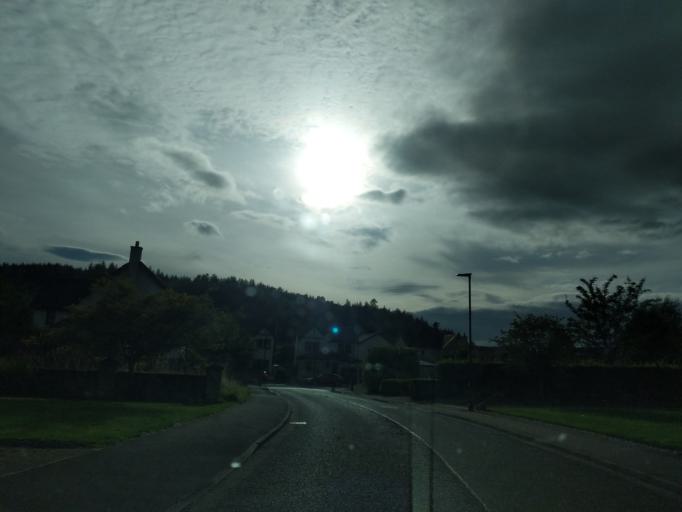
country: GB
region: Scotland
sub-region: The Scottish Borders
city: Innerleithen
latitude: 55.6394
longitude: -3.1056
